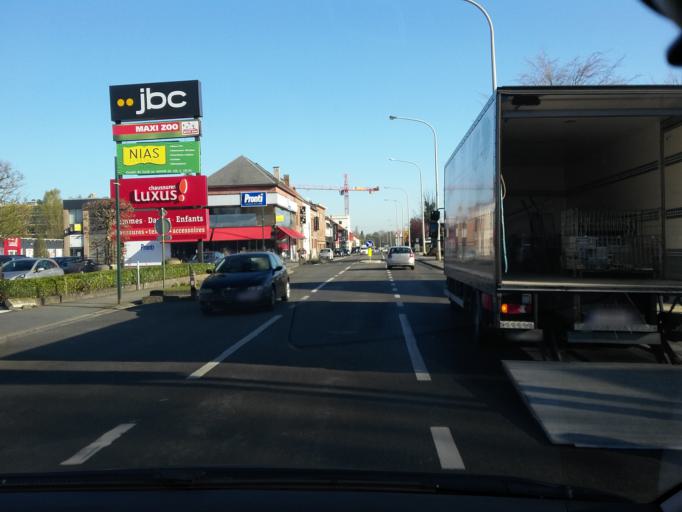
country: BE
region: Wallonia
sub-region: Province du Brabant Wallon
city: Waterloo
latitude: 50.7081
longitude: 4.4015
